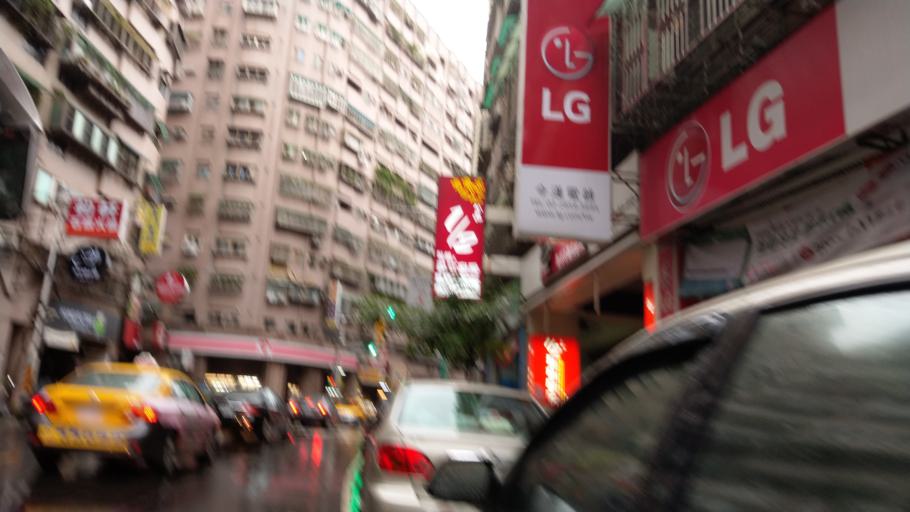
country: TW
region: Taipei
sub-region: Taipei
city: Banqiao
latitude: 24.9966
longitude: 121.4632
